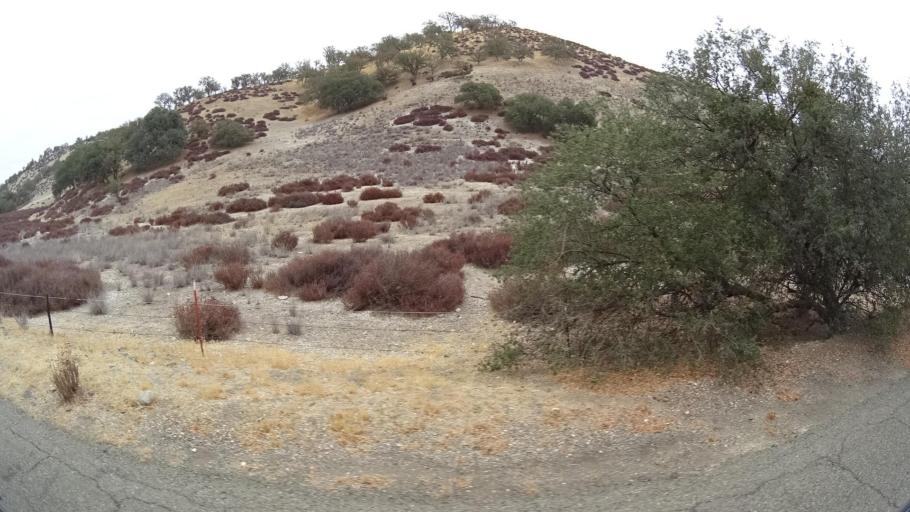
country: US
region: California
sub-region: San Luis Obispo County
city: Lake Nacimiento
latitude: 35.8839
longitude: -120.9929
